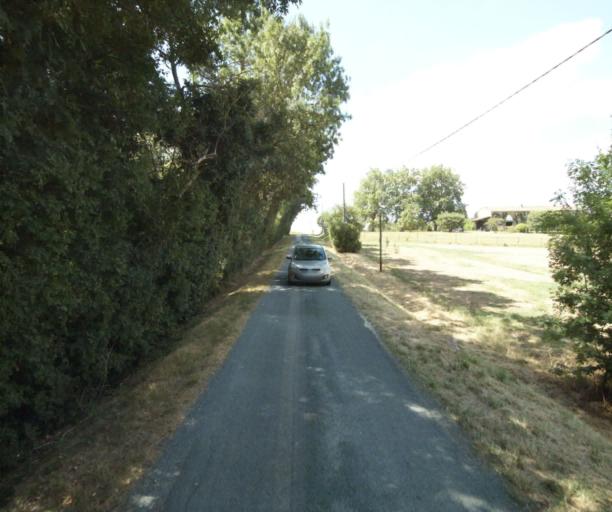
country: FR
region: Midi-Pyrenees
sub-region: Departement de la Haute-Garonne
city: Auriac-sur-Vendinelle
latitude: 43.4738
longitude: 1.8061
